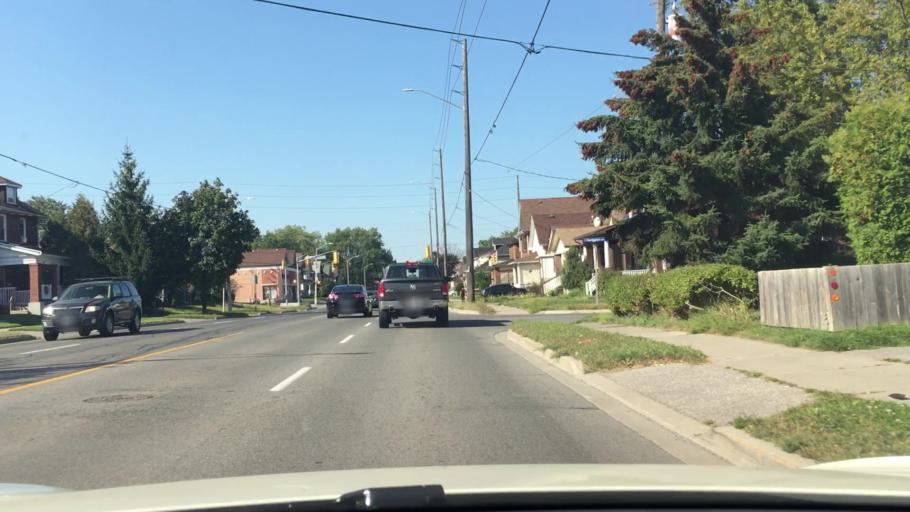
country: CA
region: Ontario
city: Oshawa
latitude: 43.8942
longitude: -78.8512
